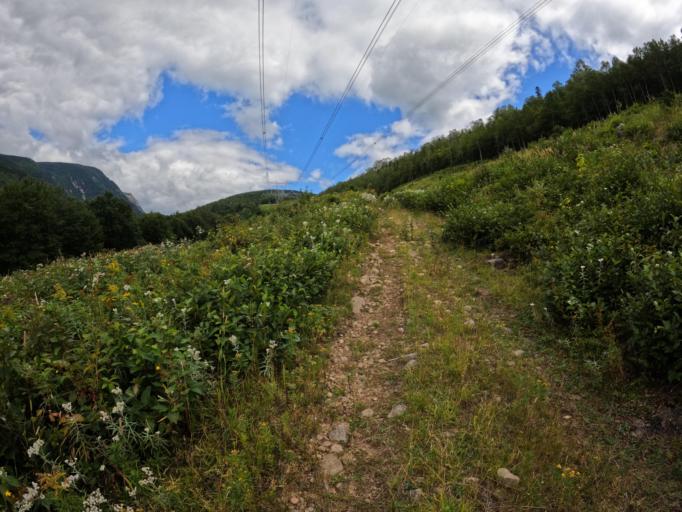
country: CA
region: Quebec
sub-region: Capitale-Nationale
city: La Malbaie
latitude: 47.8891
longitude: -70.3823
